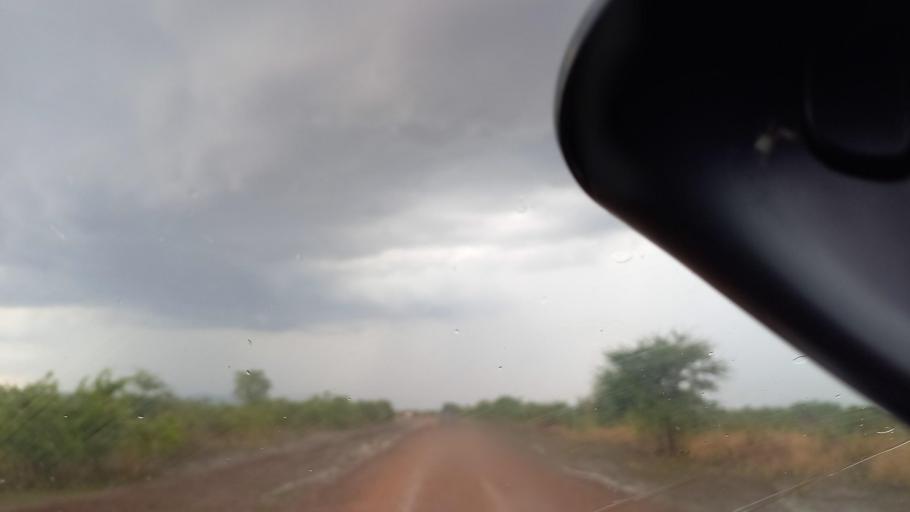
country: ZM
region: Lusaka
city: Kafue
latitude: -15.8643
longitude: 28.1754
